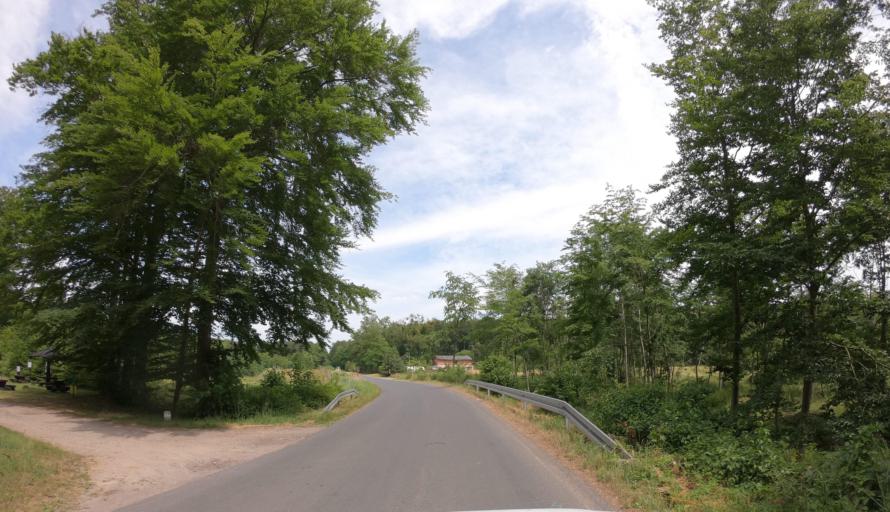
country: PL
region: West Pomeranian Voivodeship
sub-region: Powiat pyrzycki
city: Kozielice
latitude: 53.0722
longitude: 14.8178
